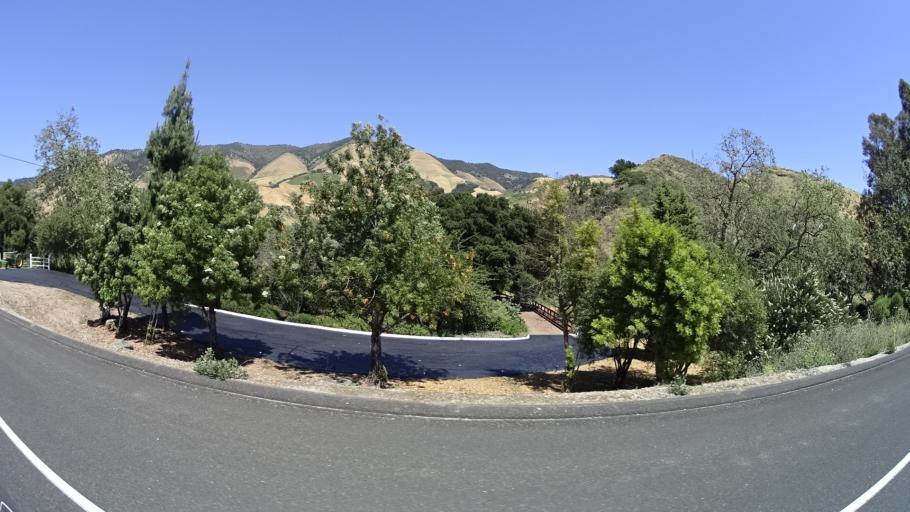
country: US
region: California
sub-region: San Luis Obispo County
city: San Luis Obispo
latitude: 35.3026
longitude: -120.6256
